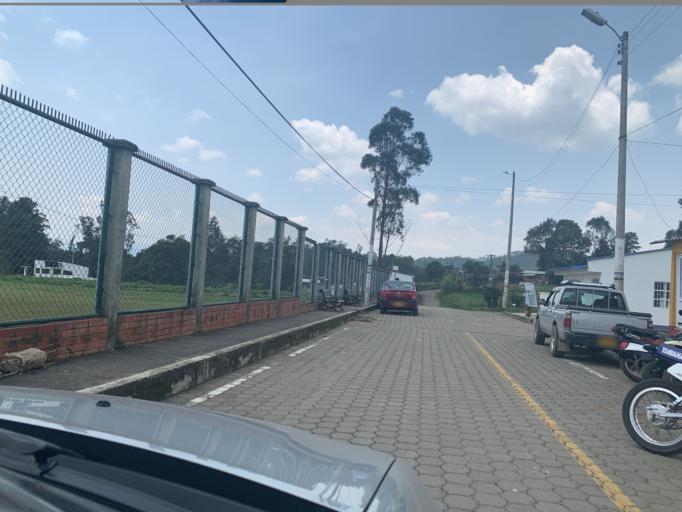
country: CO
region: Boyaca
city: Raquira
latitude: 5.5174
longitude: -73.7218
